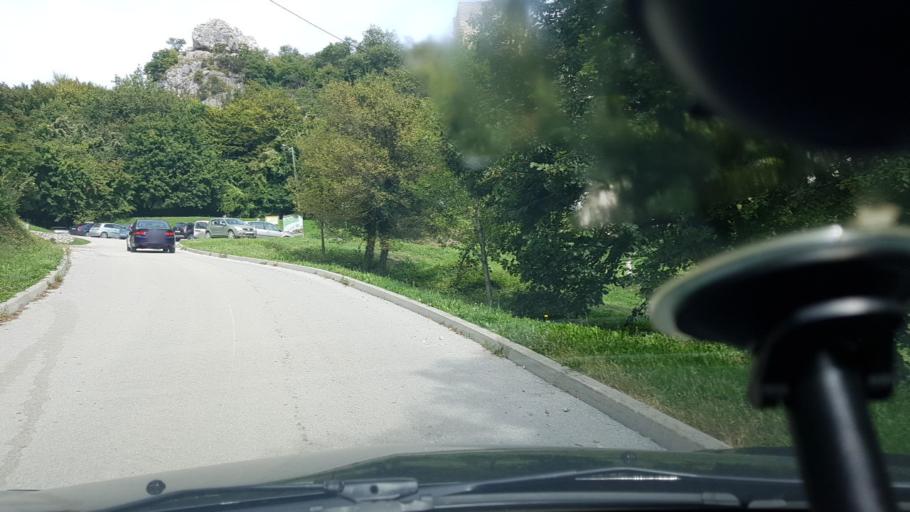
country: HR
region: Varazdinska
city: Ljubescica
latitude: 46.1321
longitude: 16.4638
